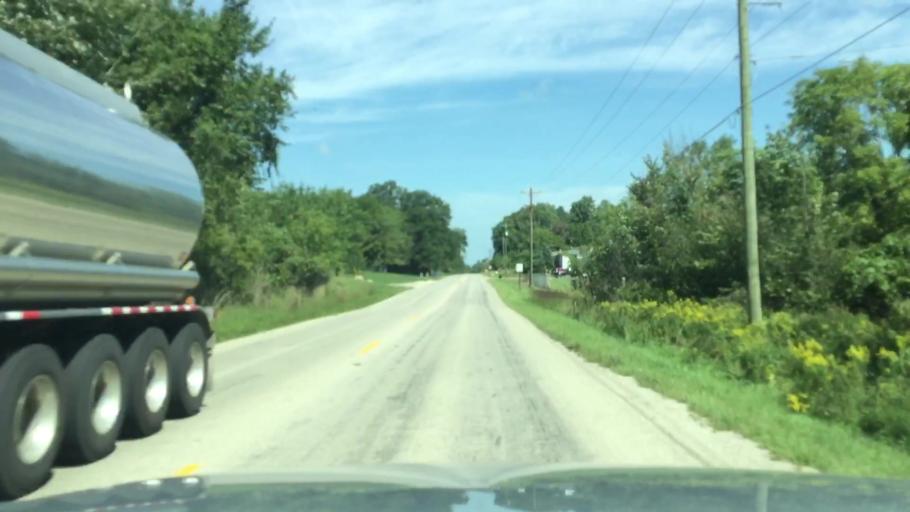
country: US
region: Michigan
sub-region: Lenawee County
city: Manitou Beach-Devils Lake
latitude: 42.0280
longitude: -84.2763
